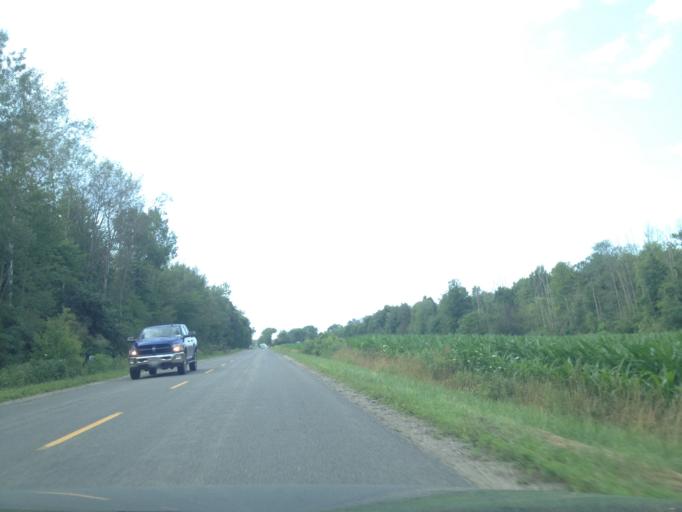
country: CA
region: Ontario
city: Aylmer
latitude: 42.6864
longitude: -80.8596
